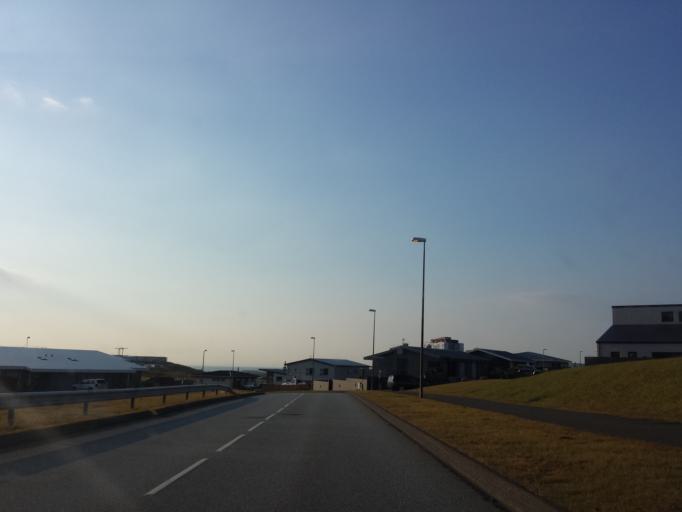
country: IS
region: Capital Region
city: Reykjavik
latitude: 64.0885
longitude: -21.8283
